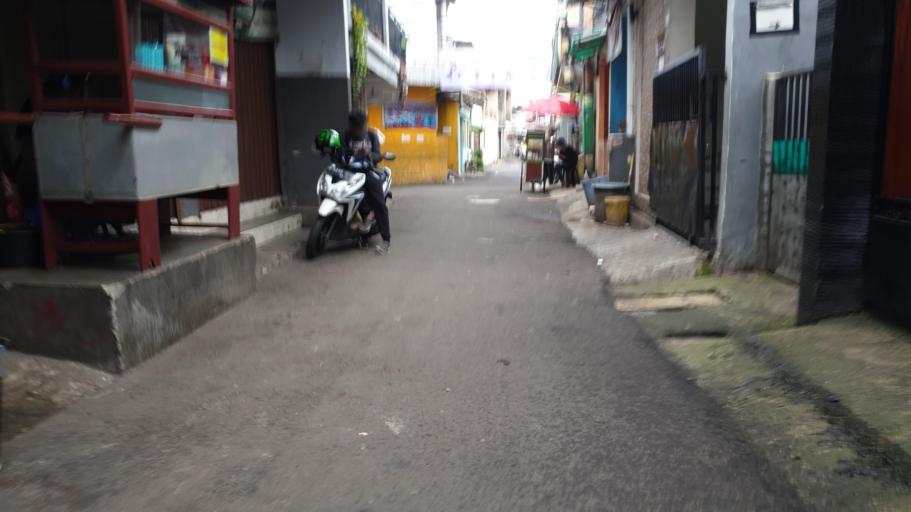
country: ID
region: Banten
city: South Tangerang
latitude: -6.2606
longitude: 106.7843
